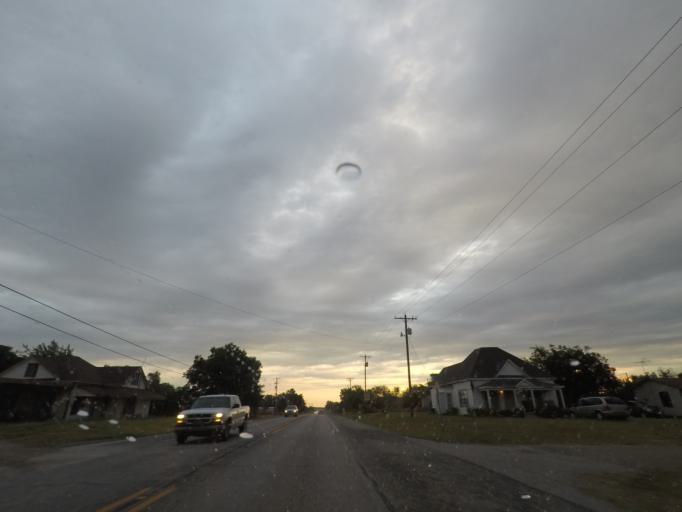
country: US
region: Texas
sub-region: Clay County
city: Henrietta
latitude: 34.0153
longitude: -98.2303
